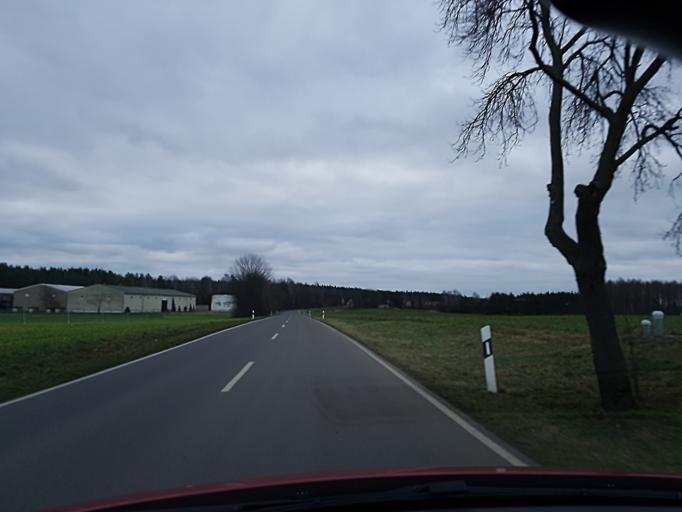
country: DE
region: Brandenburg
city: Bad Liebenwerda
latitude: 51.5567
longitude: 13.4188
